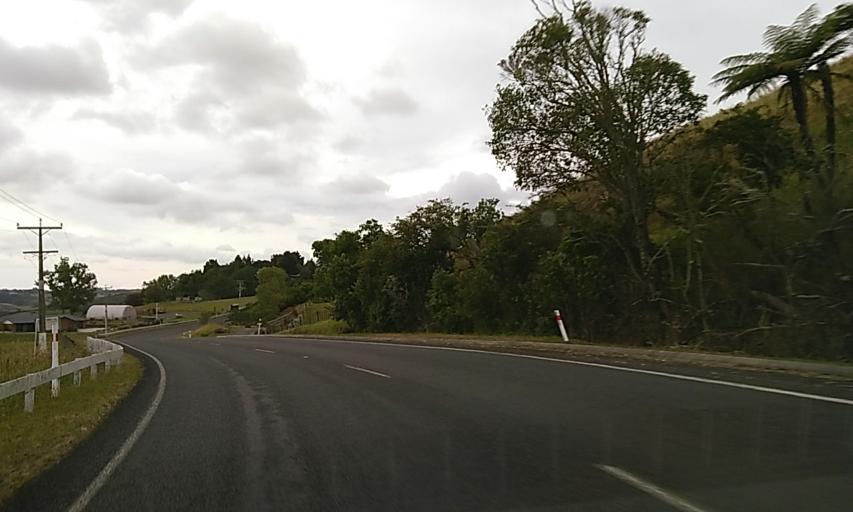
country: NZ
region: Auckland
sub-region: Auckland
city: Pukekohe East
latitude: -37.3104
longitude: 174.9375
